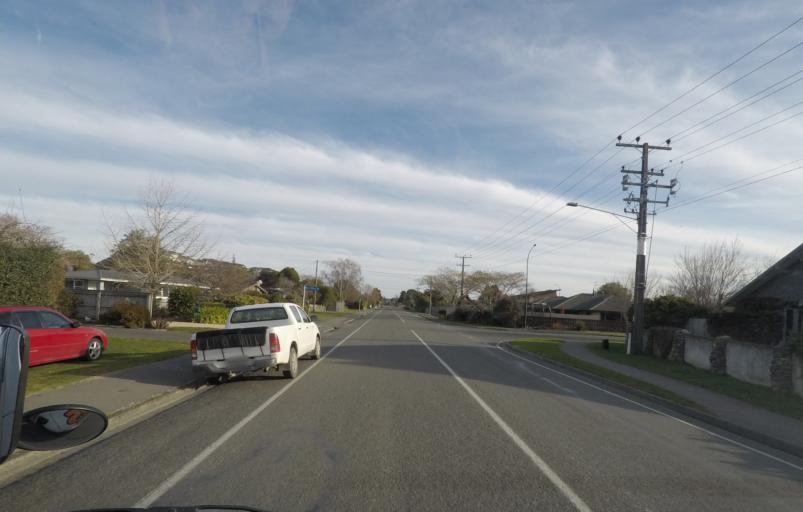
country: NZ
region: Tasman
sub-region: Tasman District
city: Brightwater
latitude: -41.3758
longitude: 173.1044
